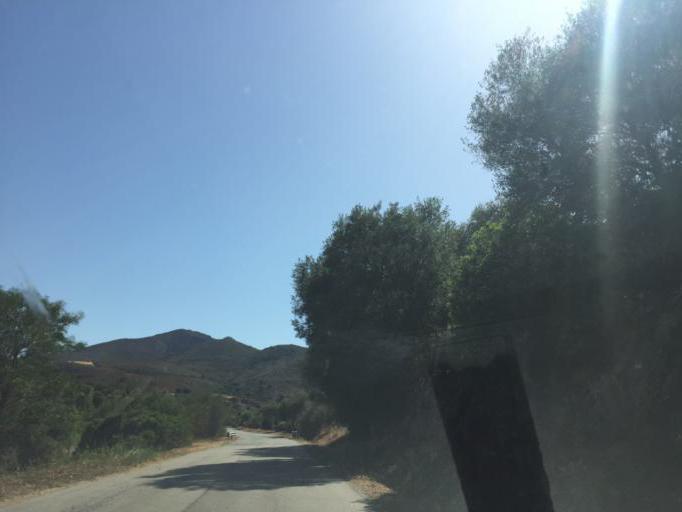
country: IT
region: Sardinia
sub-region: Provincia di Olbia-Tempio
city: San Teodoro
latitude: 40.7263
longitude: 9.6439
